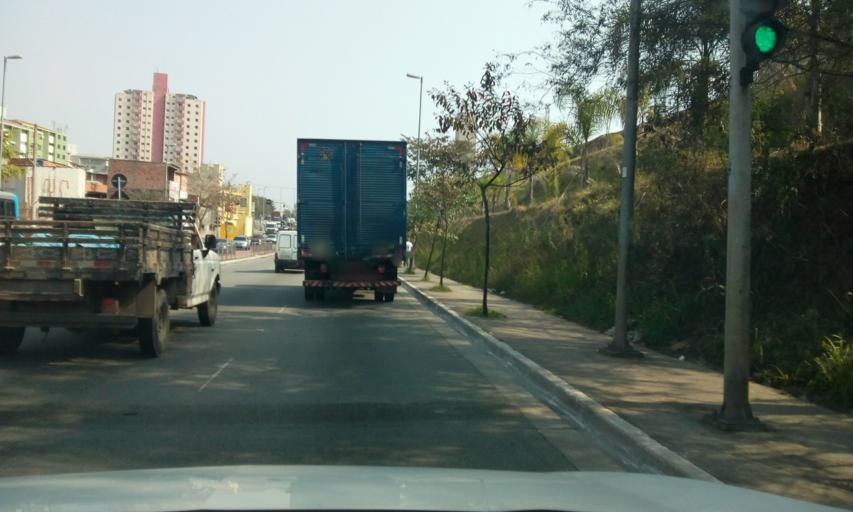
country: BR
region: Sao Paulo
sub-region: Diadema
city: Diadema
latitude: -23.7052
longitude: -46.6875
